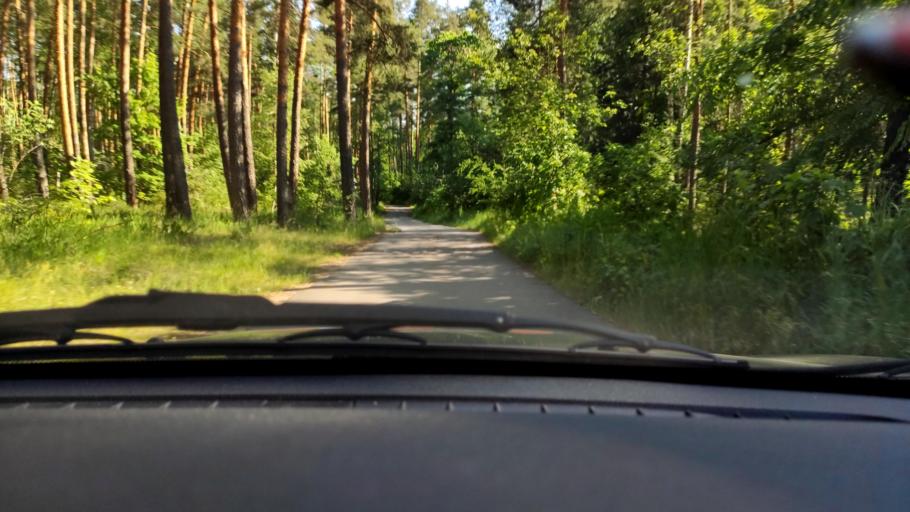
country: RU
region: Voronezj
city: Somovo
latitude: 51.8034
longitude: 39.3801
